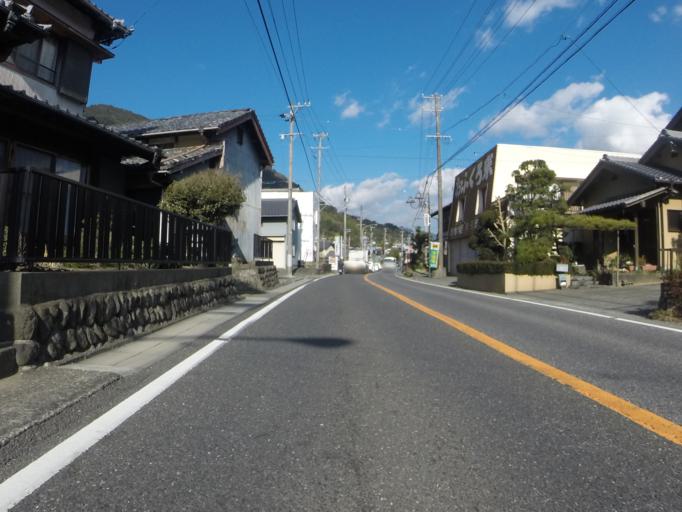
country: JP
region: Shizuoka
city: Fujinomiya
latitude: 35.0831
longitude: 138.5143
